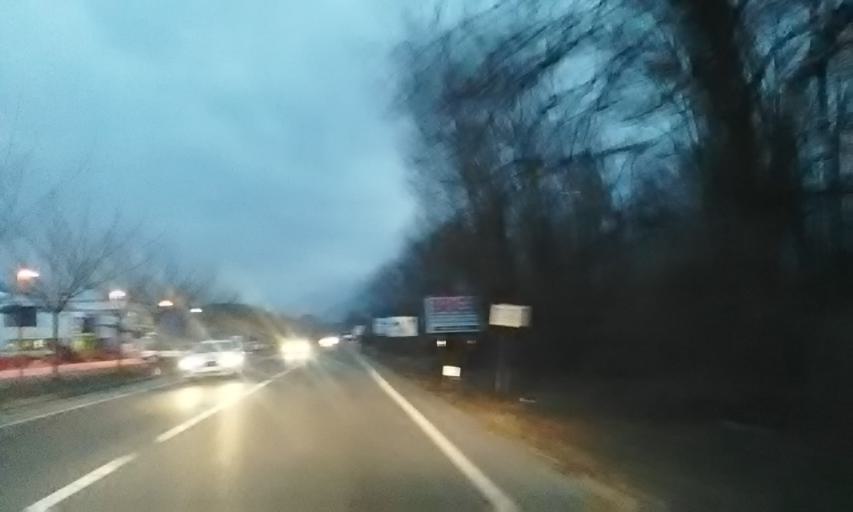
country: IT
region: Piedmont
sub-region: Provincia di Torino
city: Montalto Dora
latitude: 45.4983
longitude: 7.8582
